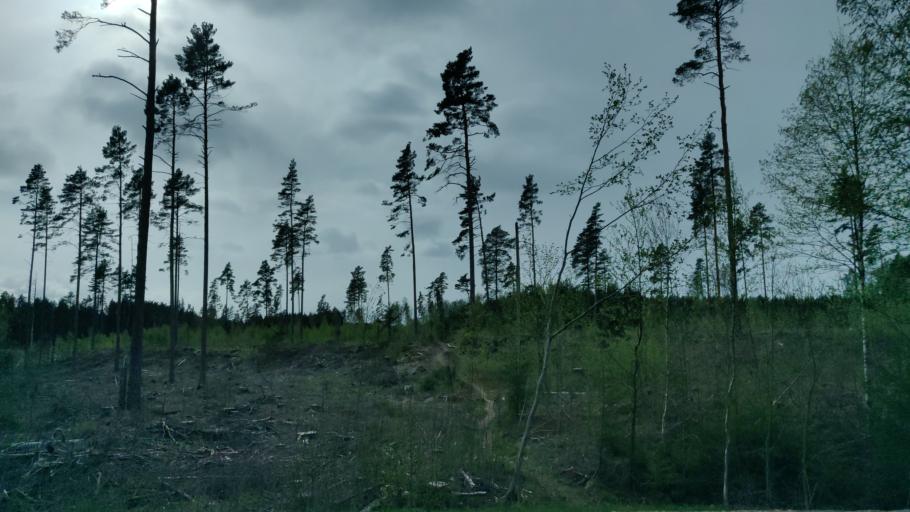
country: SE
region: Vaermland
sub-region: Forshaga Kommun
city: Deje
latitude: 59.6381
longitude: 13.4432
